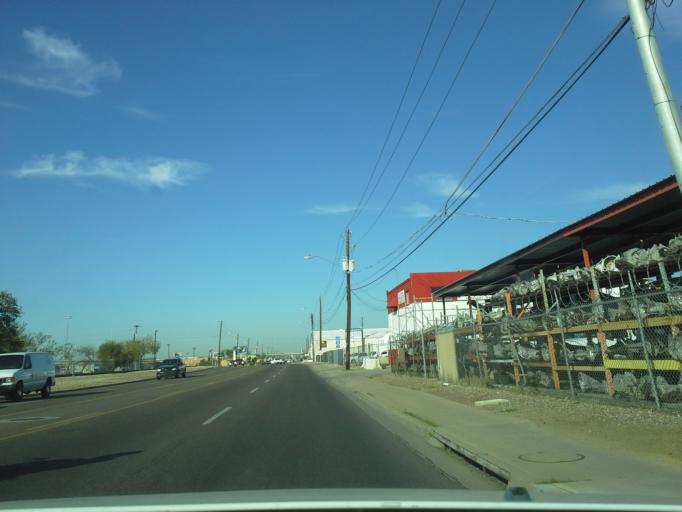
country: US
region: Arizona
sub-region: Maricopa County
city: Phoenix
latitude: 33.4530
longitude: -112.1000
